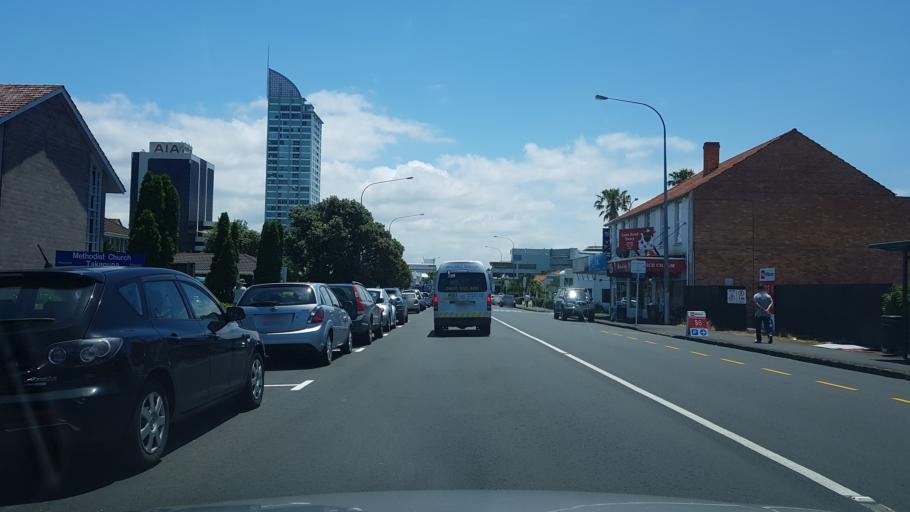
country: NZ
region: Auckland
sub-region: Auckland
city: North Shore
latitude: -36.7921
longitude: 174.7746
